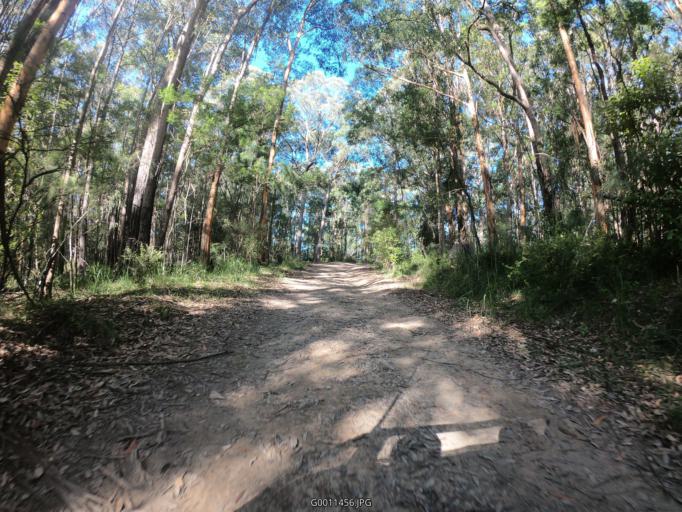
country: AU
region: New South Wales
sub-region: Lake Macquarie Shire
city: Cooranbong
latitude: -33.0277
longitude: 151.3055
